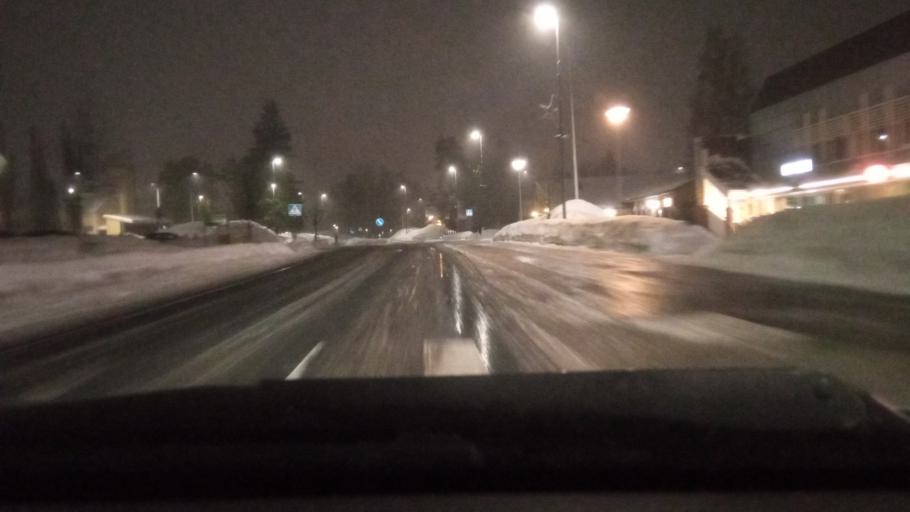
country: FI
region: Southern Ostrobothnia
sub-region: Jaerviseutu
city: Alajaervi
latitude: 63.0010
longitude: 23.8152
